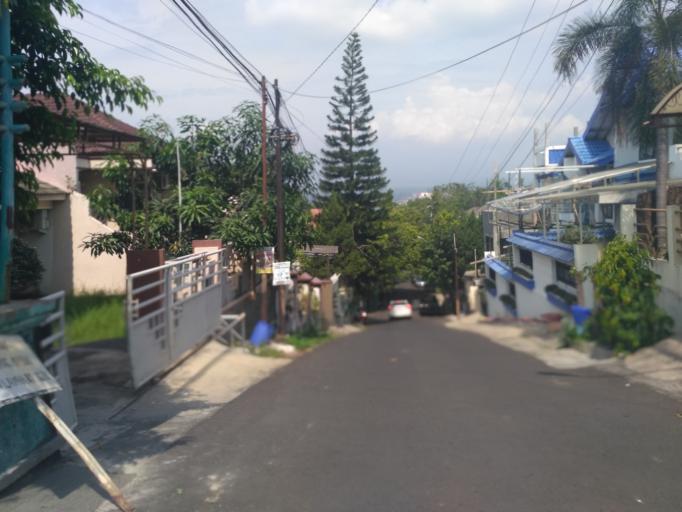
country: ID
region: Central Java
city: Semarang
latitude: -7.0470
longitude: 110.4254
